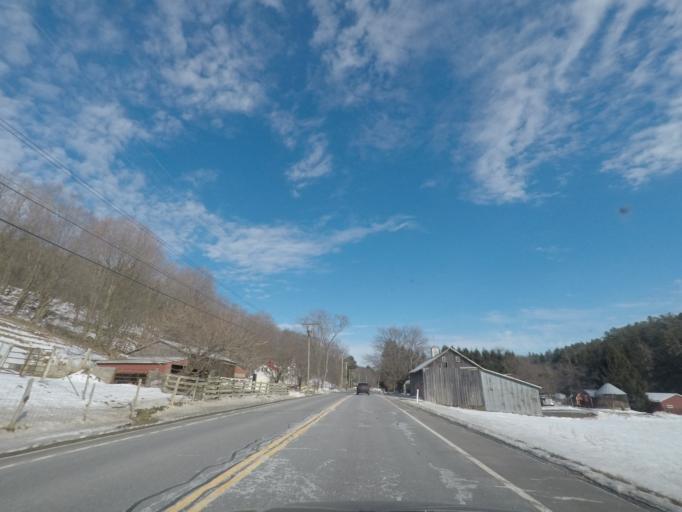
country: US
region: New York
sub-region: Albany County
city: Altamont
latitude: 42.7780
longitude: -74.0720
